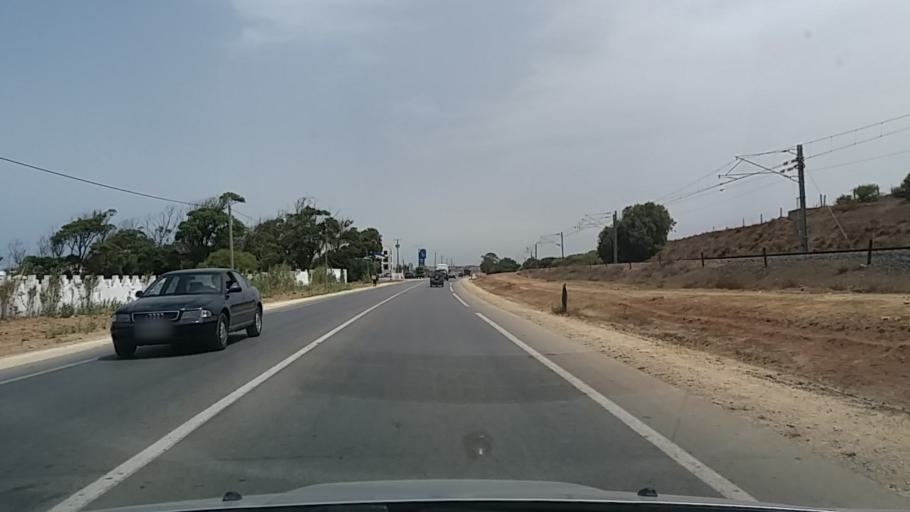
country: MA
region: Tanger-Tetouan
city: Asilah
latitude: 35.4943
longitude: -6.0172
